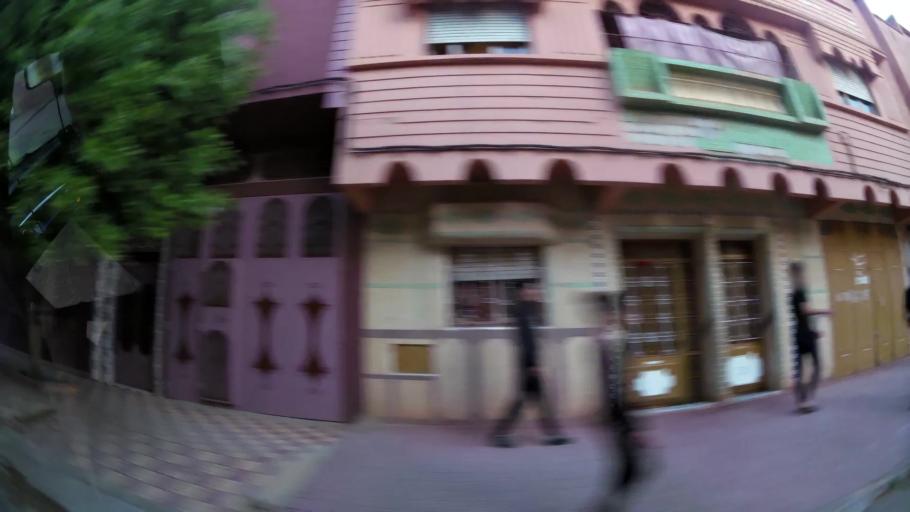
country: MA
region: Oriental
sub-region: Berkane-Taourirt
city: Berkane
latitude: 34.9129
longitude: -2.3163
